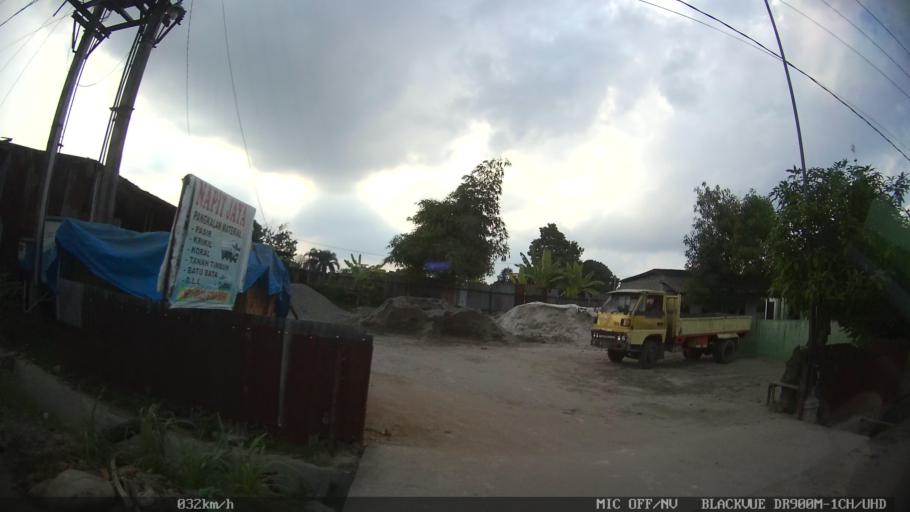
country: ID
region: North Sumatra
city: Medan
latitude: 3.5891
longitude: 98.7410
